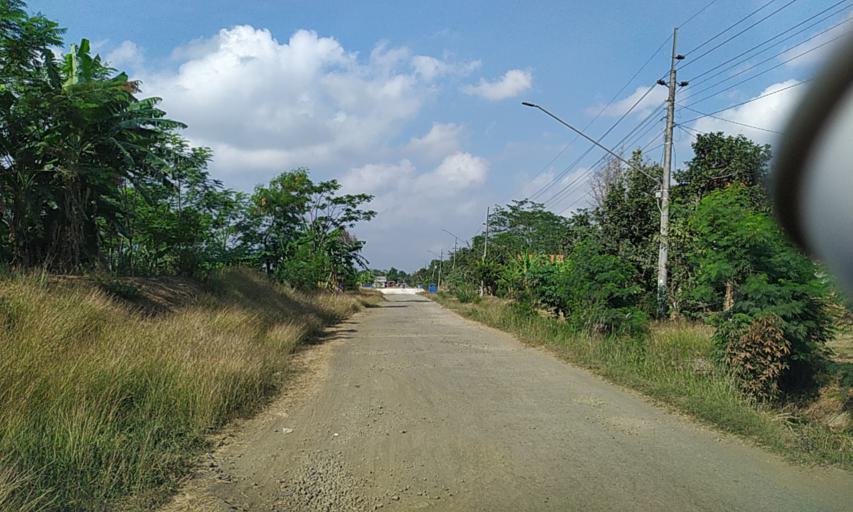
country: ID
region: Central Java
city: Sidakaya
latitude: -7.6161
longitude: 108.8597
